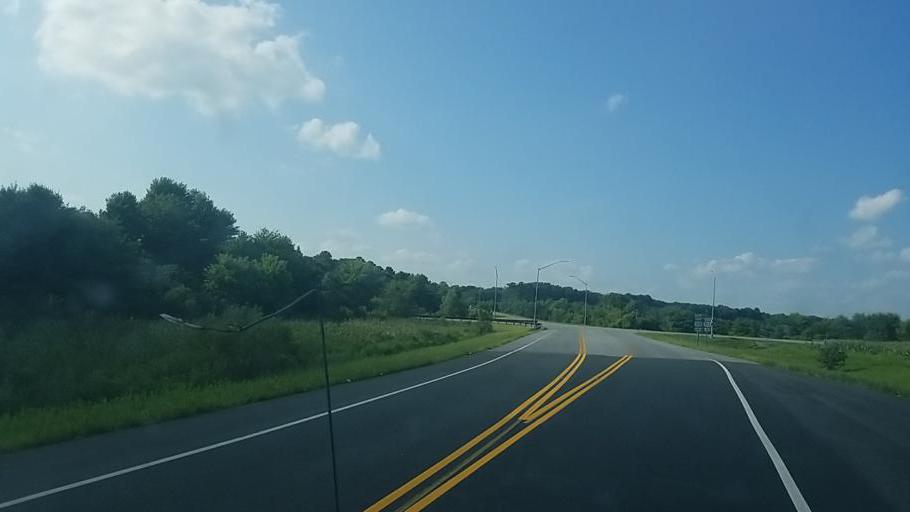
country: US
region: Maryland
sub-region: Worcester County
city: Ocean Pines
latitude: 38.3895
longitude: -75.2023
